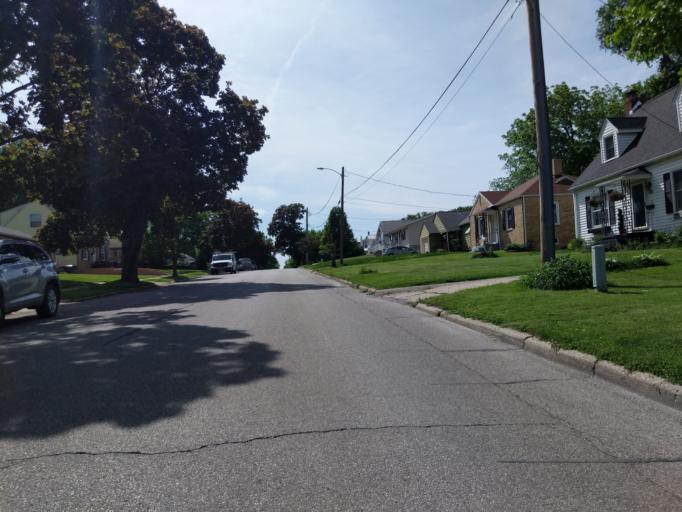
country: US
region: Iowa
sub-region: Linn County
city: Cedar Rapids
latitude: 42.0171
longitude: -91.6357
